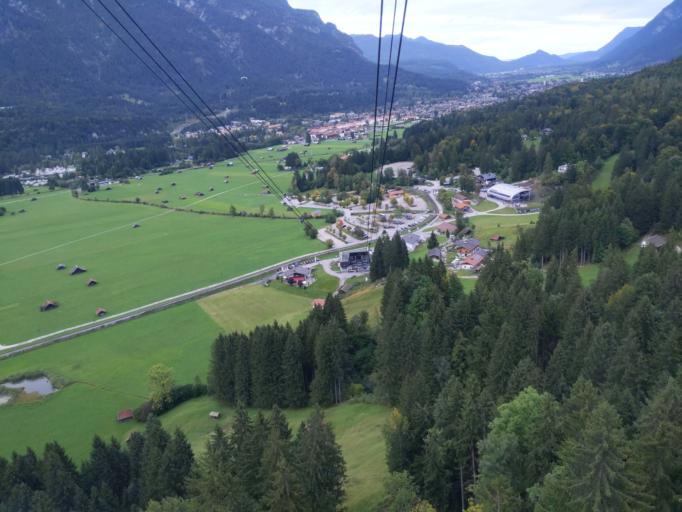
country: DE
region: Bavaria
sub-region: Upper Bavaria
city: Grainau
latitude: 47.4672
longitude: 11.0602
